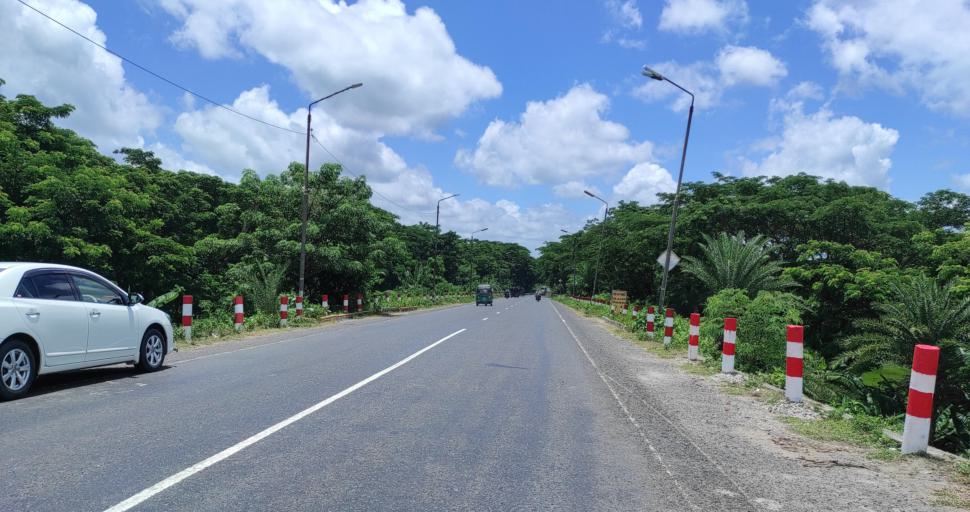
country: BD
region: Barisal
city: Gaurnadi
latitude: 22.8235
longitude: 90.2648
